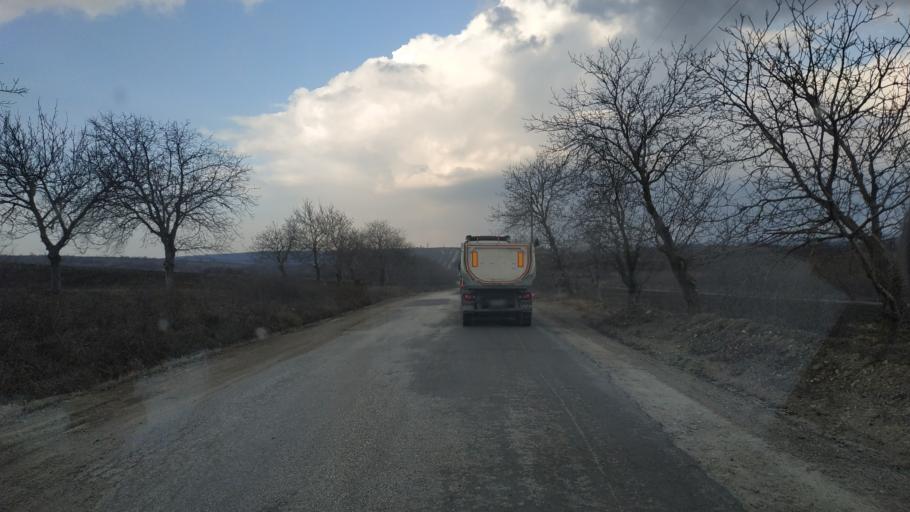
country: MD
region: Anenii Noi
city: Anenii Noi
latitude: 46.9709
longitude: 29.2852
